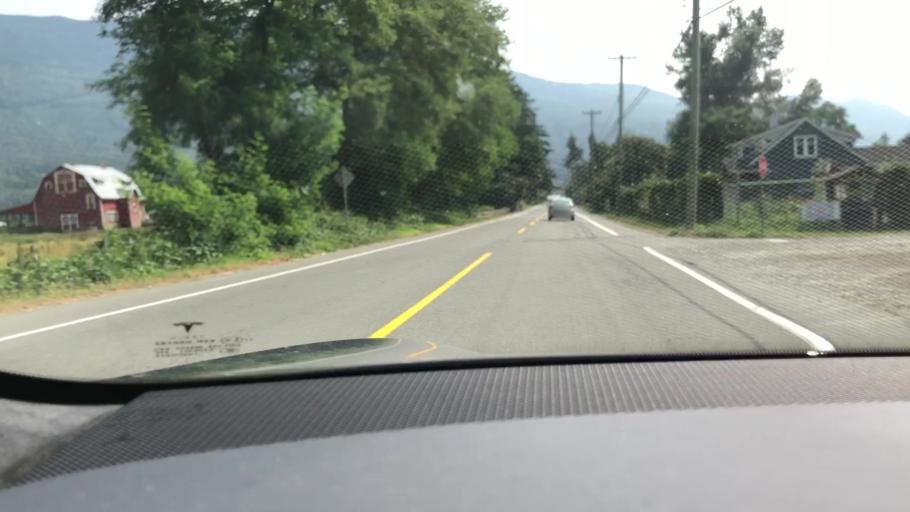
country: CA
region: British Columbia
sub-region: Fraser Valley Regional District
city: Chilliwack
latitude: 49.0877
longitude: -122.0648
